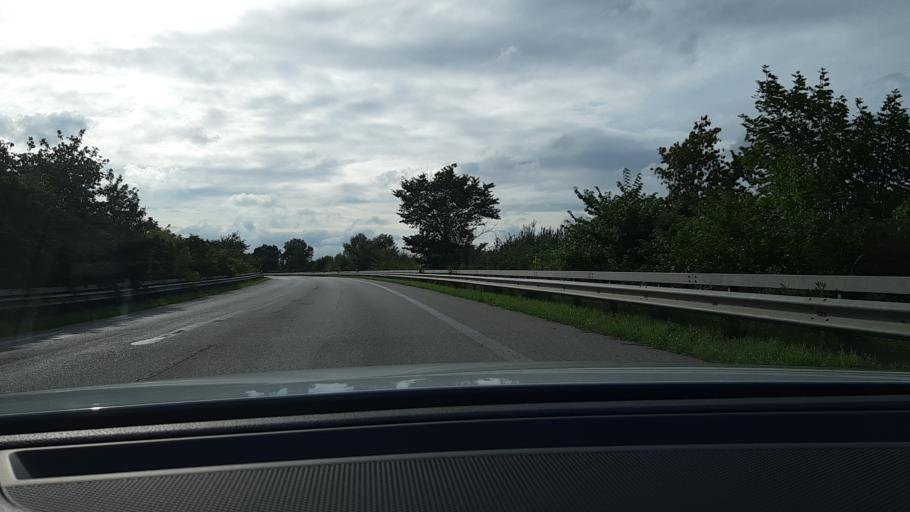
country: DE
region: Schleswig-Holstein
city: Stockelsdorf
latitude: 53.8923
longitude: 10.6326
